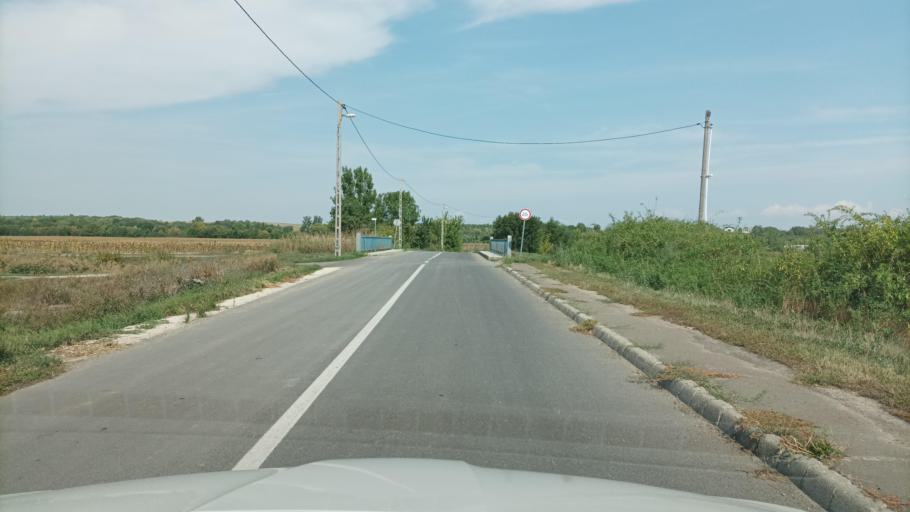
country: HU
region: Pest
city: Galgaheviz
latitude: 47.6270
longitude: 19.5537
